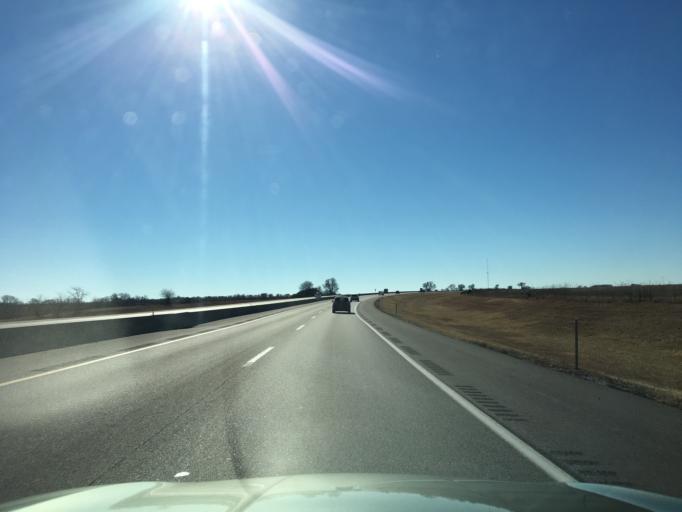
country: US
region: Kansas
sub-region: Sumner County
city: Belle Plaine
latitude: 37.3478
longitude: -97.3220
